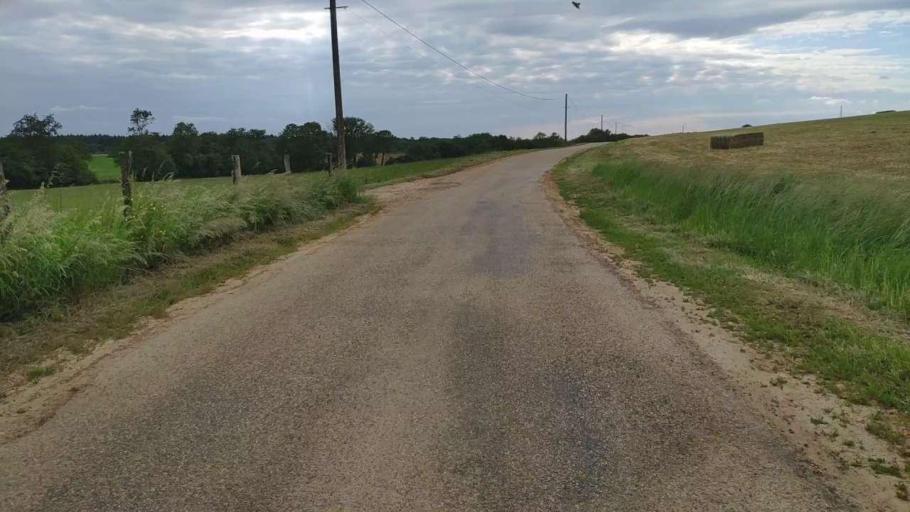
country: FR
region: Franche-Comte
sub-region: Departement du Jura
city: Bletterans
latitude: 46.7985
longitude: 5.5438
